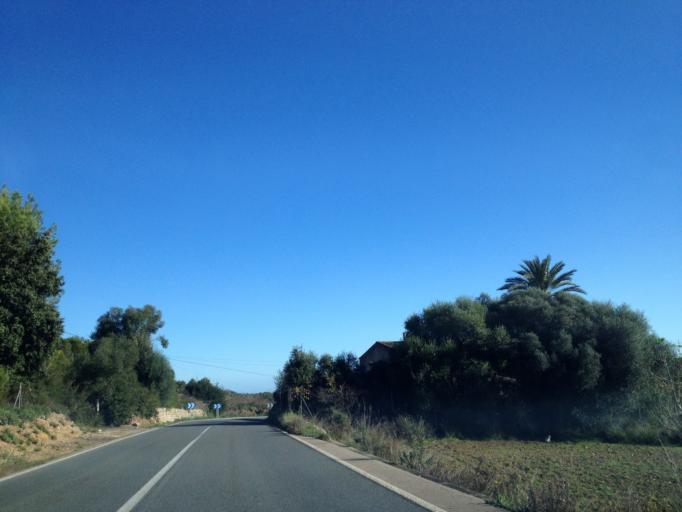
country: ES
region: Balearic Islands
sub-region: Illes Balears
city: Sineu
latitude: 39.6546
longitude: 3.0326
